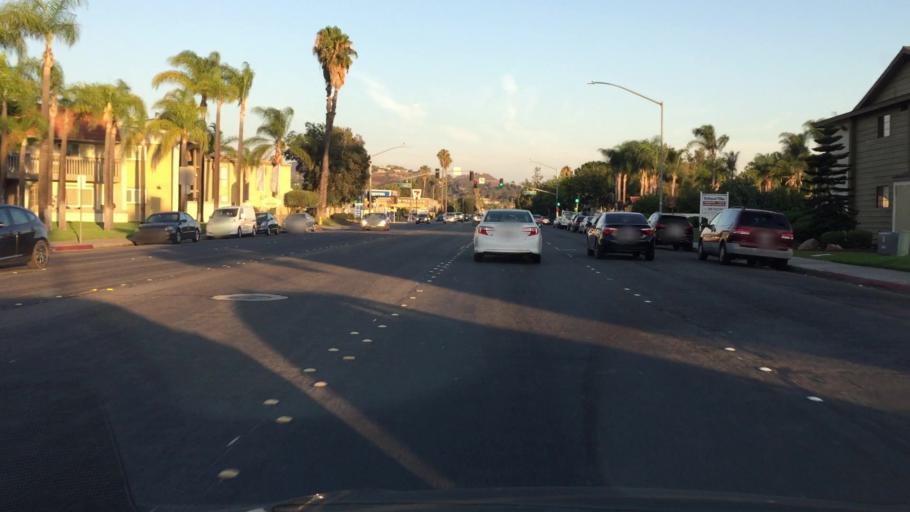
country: US
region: California
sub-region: San Diego County
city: Bostonia
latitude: 32.7934
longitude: -116.9347
